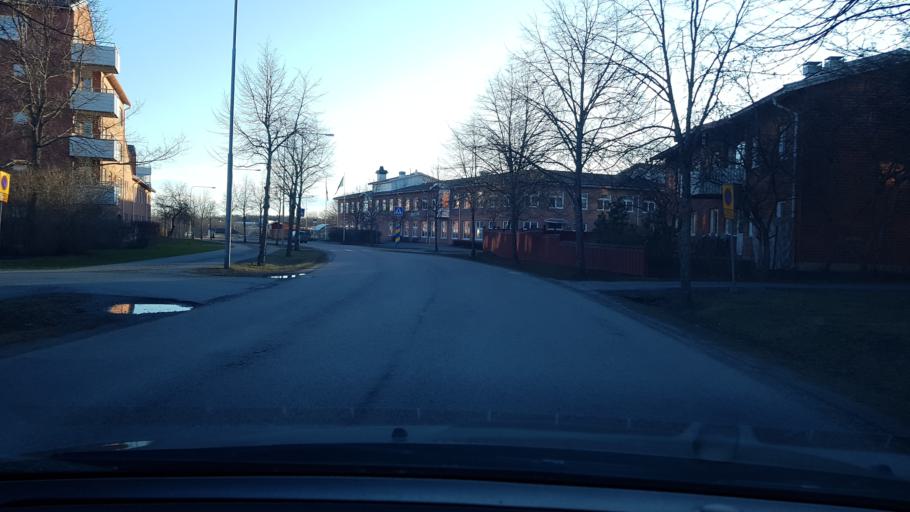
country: SE
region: Stockholm
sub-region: Norrtalje Kommun
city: Norrtalje
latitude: 59.7480
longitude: 18.6927
